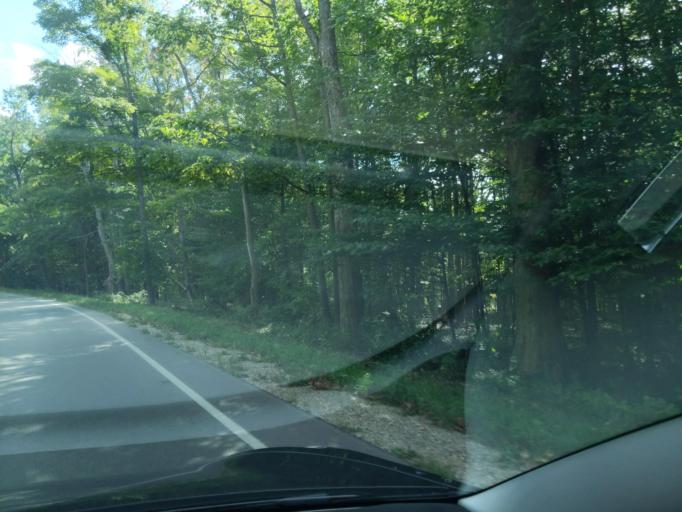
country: US
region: Michigan
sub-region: Antrim County
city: Bellaire
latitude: 45.0431
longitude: -85.3040
